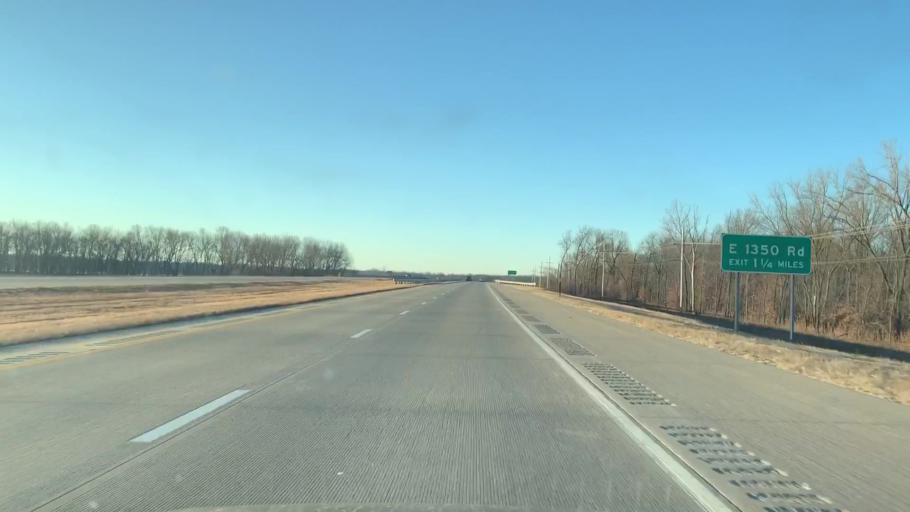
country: US
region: Kansas
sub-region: Linn County
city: Pleasanton
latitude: 38.2382
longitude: -94.6905
